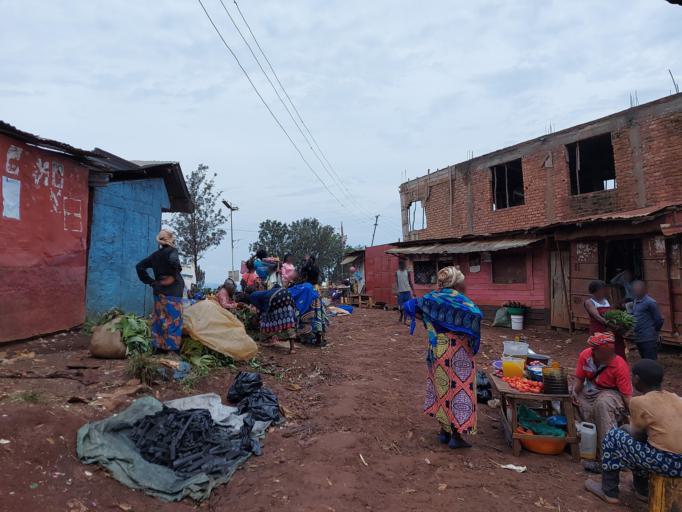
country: CD
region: South Kivu
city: Bukavu
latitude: -2.4832
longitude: 28.8193
